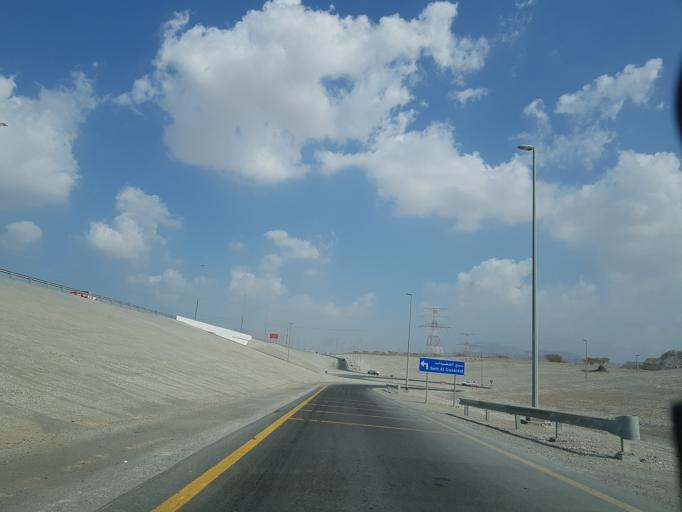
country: AE
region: Ra's al Khaymah
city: Ras al-Khaimah
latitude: 25.7616
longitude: 56.0223
